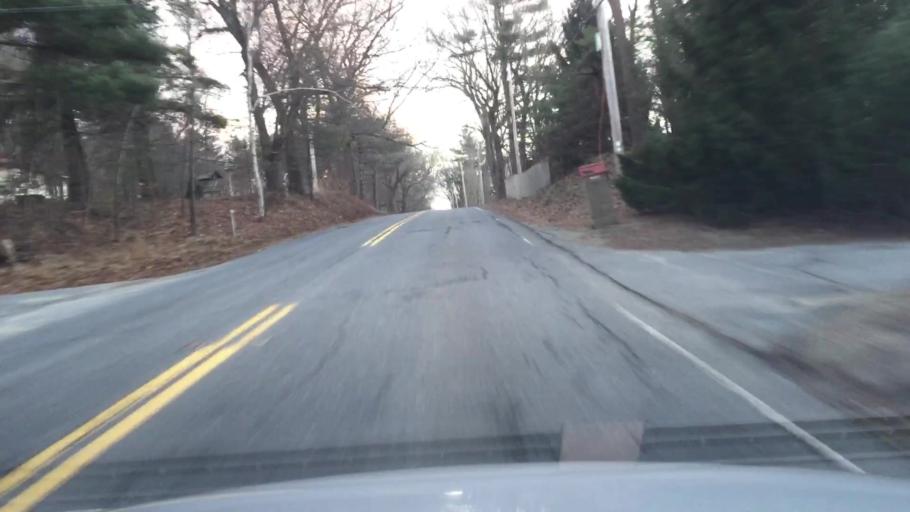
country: US
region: Massachusetts
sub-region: Worcester County
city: Sterling
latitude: 42.4124
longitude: -71.8010
